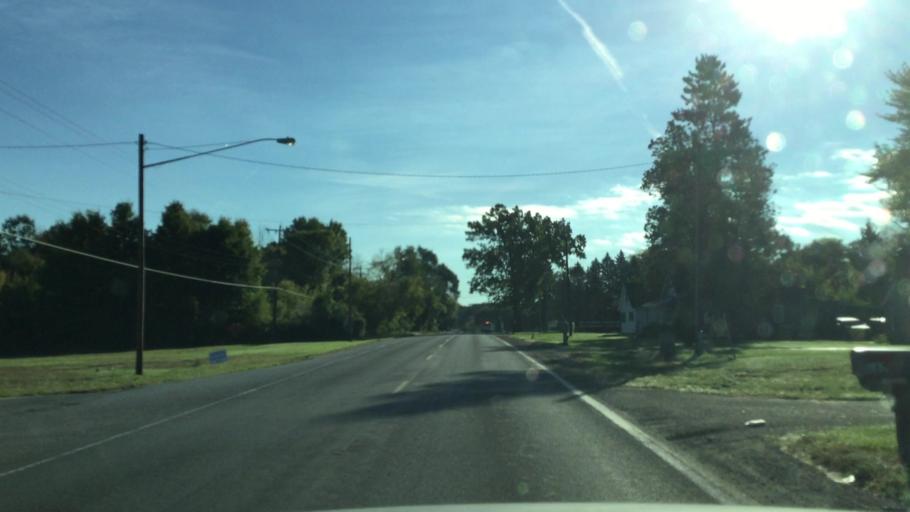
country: US
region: Michigan
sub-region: Genesee County
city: Beecher
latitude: 43.0898
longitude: -83.7398
